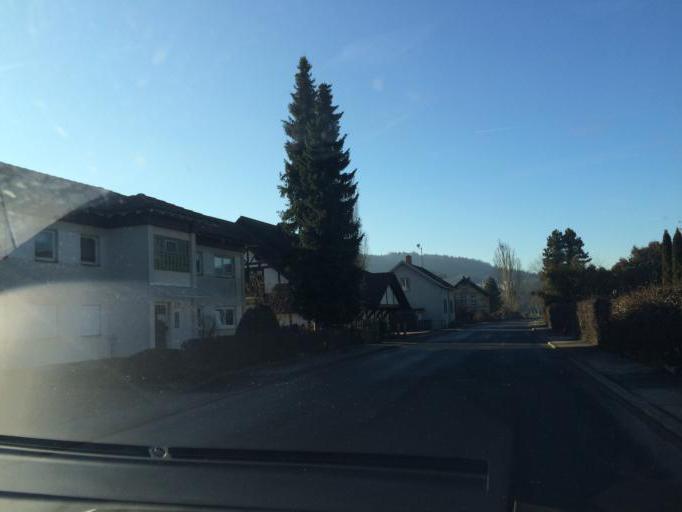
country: DE
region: Baden-Wuerttemberg
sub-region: Freiburg Region
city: Busingen
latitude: 47.6863
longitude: 8.6675
